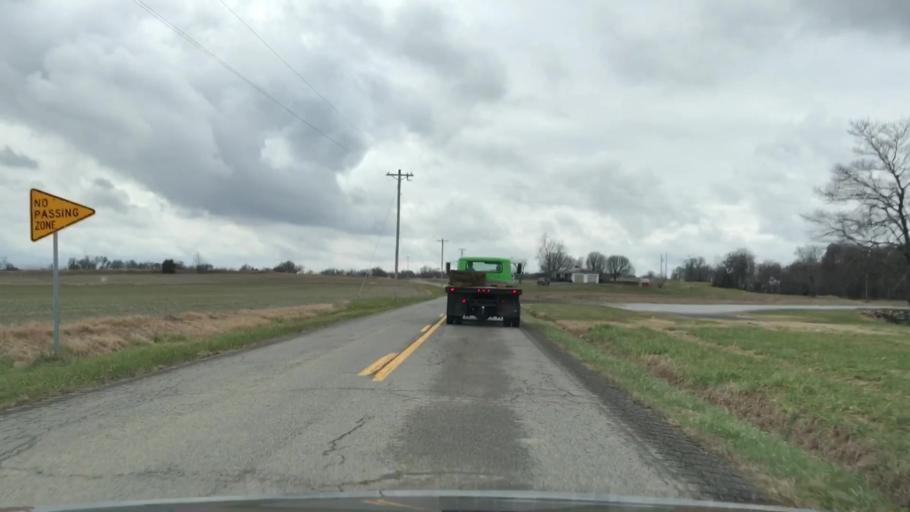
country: US
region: Kentucky
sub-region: Webster County
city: Sebree
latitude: 37.5079
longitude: -87.4264
